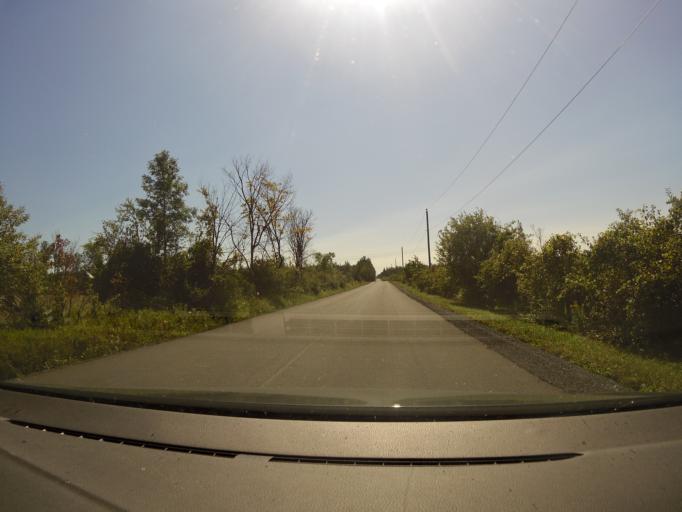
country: CA
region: Ontario
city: Bells Corners
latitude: 45.2568
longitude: -75.9965
